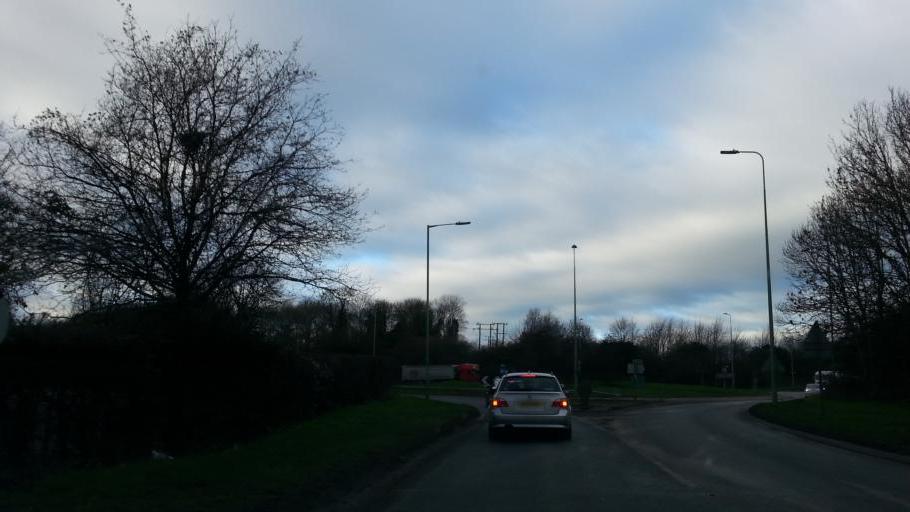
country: GB
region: England
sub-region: Suffolk
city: Bury St Edmunds
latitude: 52.2614
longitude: 0.7262
